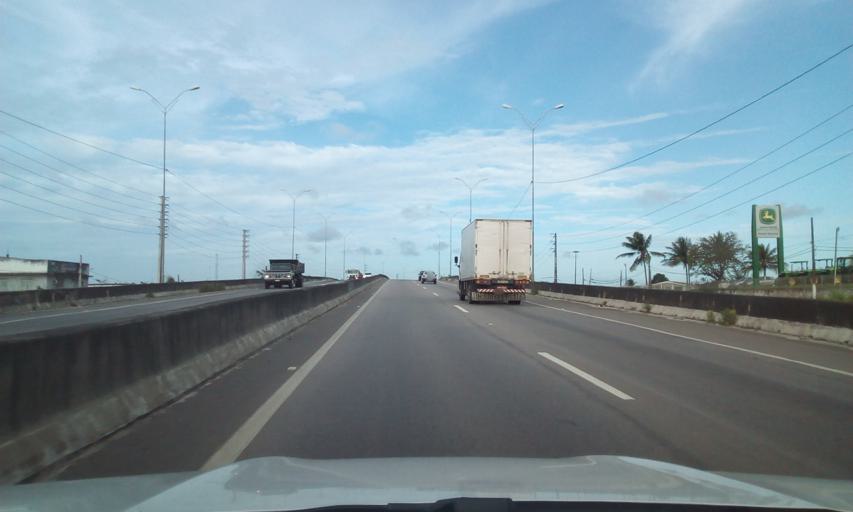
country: BR
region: Paraiba
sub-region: Bayeux
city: Bayeux
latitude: -7.1308
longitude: -34.9338
